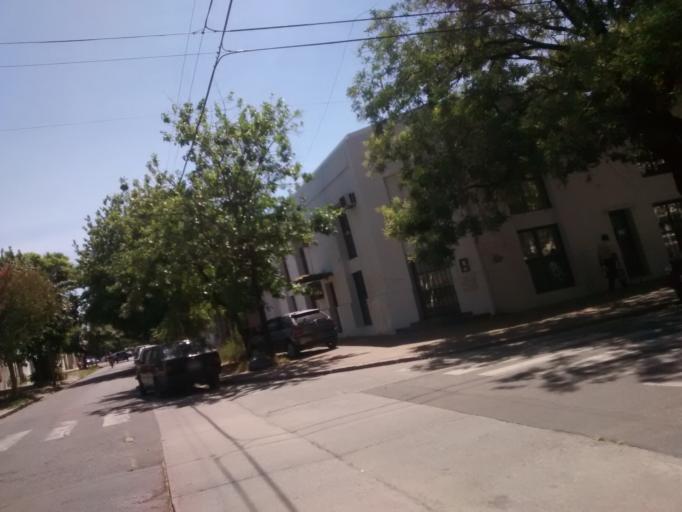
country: AR
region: Buenos Aires
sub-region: Partido de La Plata
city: La Plata
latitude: -34.9080
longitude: -57.9565
